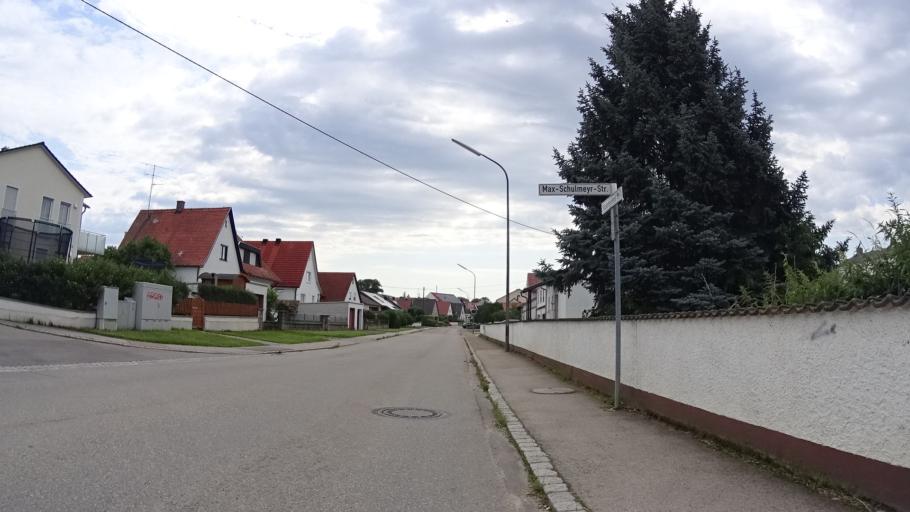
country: DE
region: Bavaria
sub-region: Upper Bavaria
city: Wettstetten
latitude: 48.8260
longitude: 11.4091
